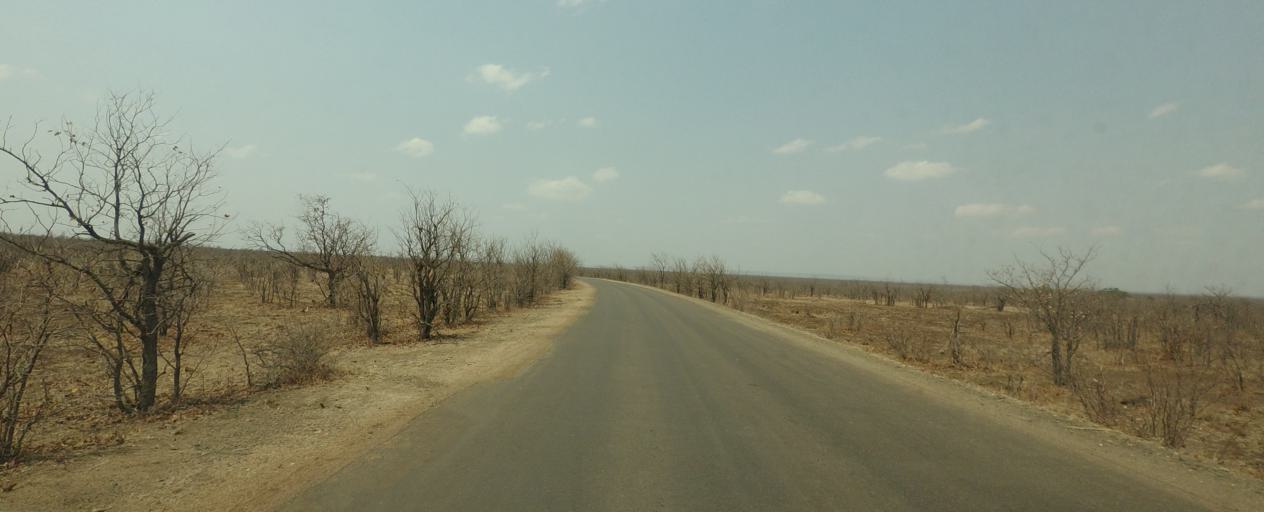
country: ZA
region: Limpopo
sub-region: Mopani District Municipality
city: Phalaborwa
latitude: -23.5188
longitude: 31.4040
